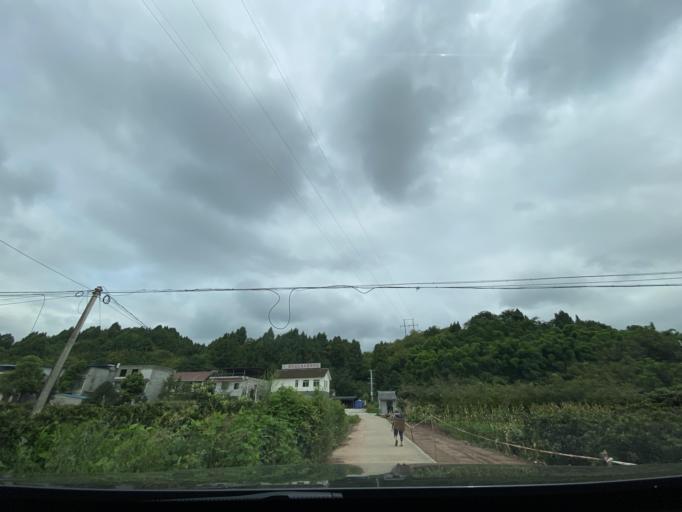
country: CN
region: Sichuan
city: Jiancheng
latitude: 30.4032
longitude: 104.5737
